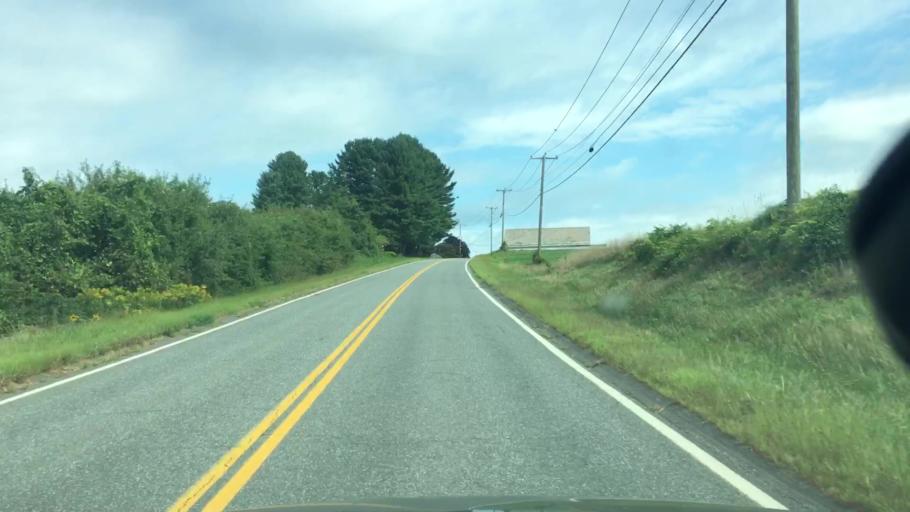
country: US
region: Massachusetts
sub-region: Franklin County
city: Shelburne
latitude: 42.6127
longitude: -72.6724
